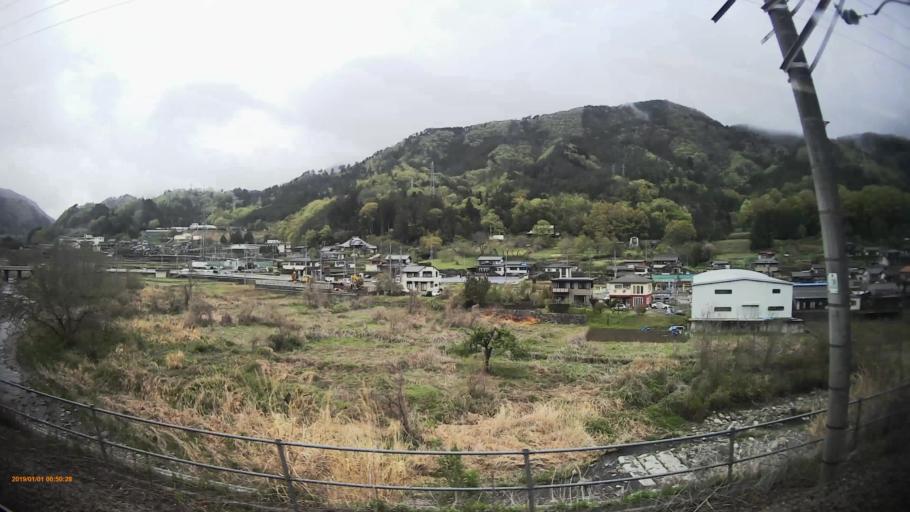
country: JP
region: Yamanashi
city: Otsuki
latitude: 35.5977
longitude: 138.8916
